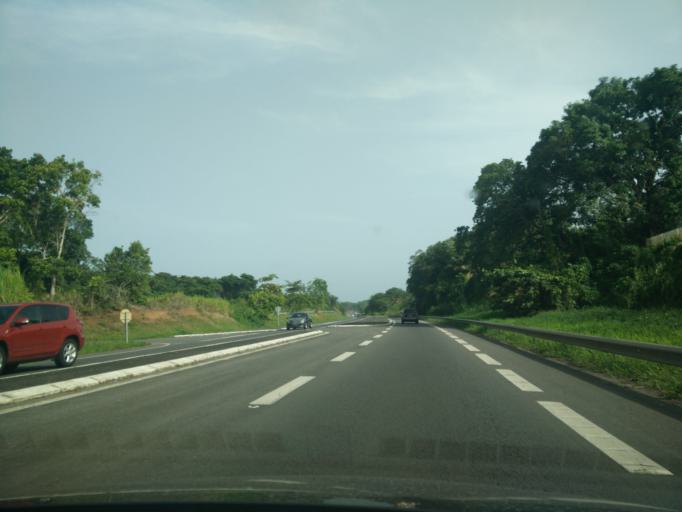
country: GP
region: Guadeloupe
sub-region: Guadeloupe
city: Petit-Bourg
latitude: 16.1587
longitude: -61.5862
